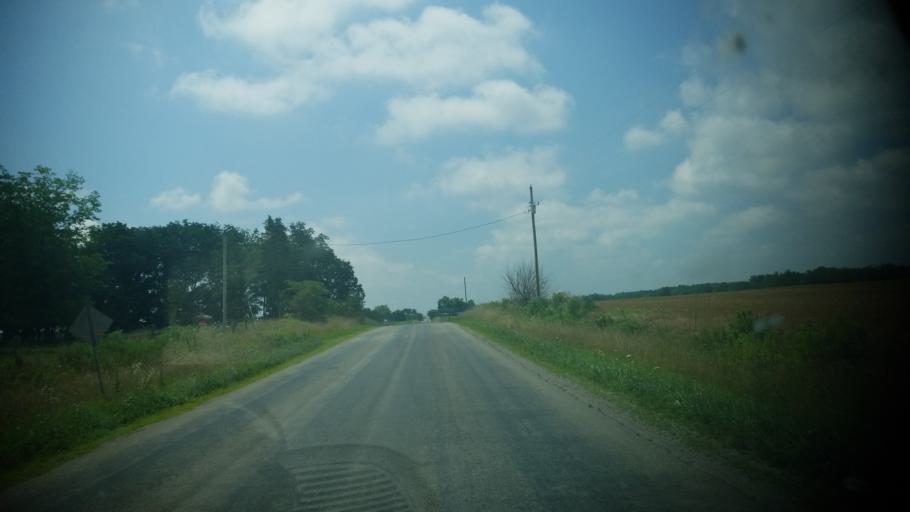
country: US
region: Illinois
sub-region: Wayne County
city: Fairfield
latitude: 38.5209
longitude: -88.3485
